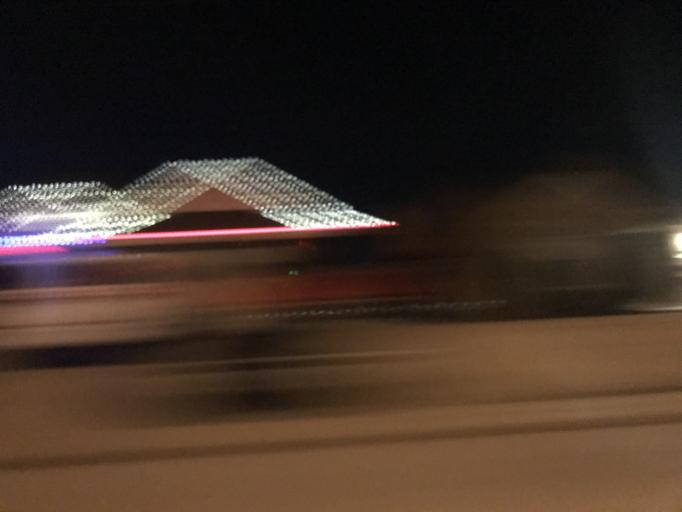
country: US
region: Texas
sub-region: Taylor County
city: Abilene
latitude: 32.3808
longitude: -99.7207
